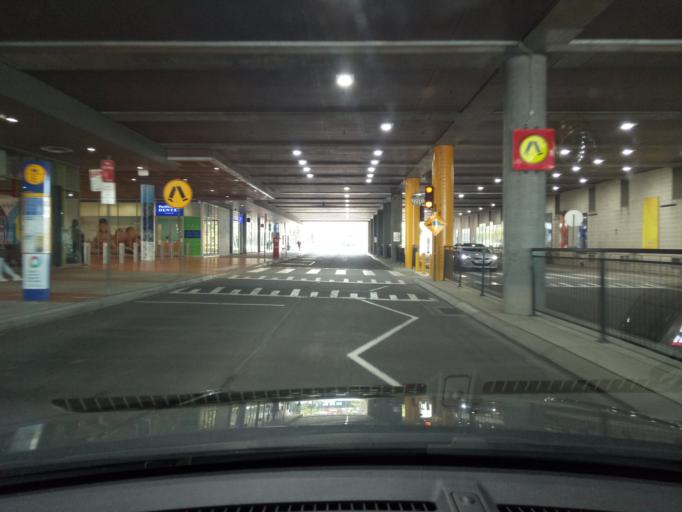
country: AU
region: New South Wales
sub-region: Gosford Shire
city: Erina
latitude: -33.4376
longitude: 151.3922
